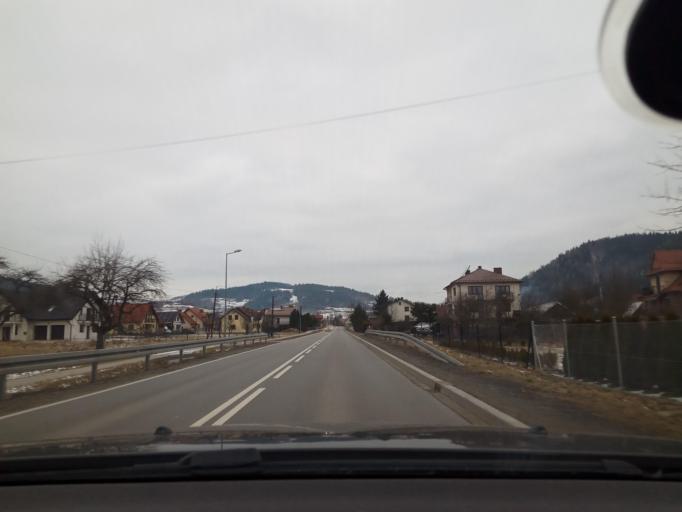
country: PL
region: Lesser Poland Voivodeship
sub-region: Powiat limanowski
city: Kamienica
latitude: 49.5767
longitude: 20.3374
